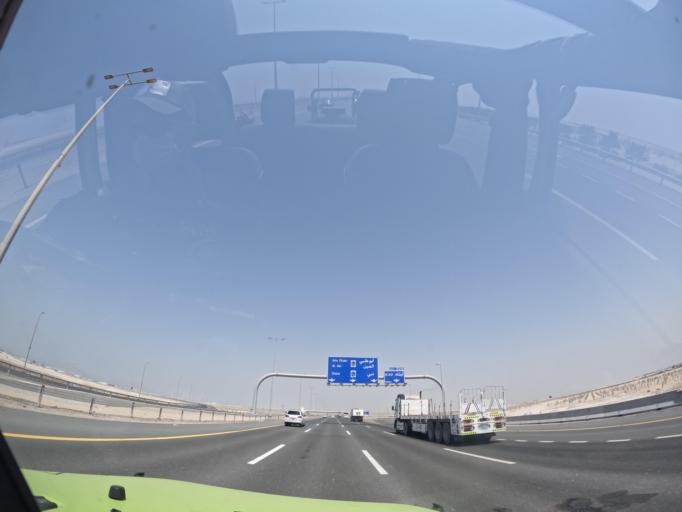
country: AE
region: Abu Dhabi
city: Abu Dhabi
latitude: 24.2414
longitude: 54.4680
